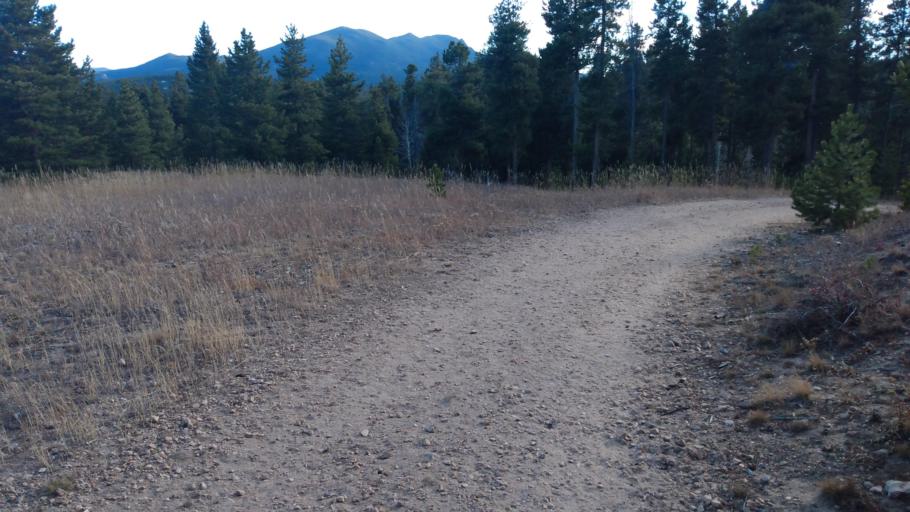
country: US
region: Colorado
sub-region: Boulder County
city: Nederland
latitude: 39.9591
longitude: -105.4481
